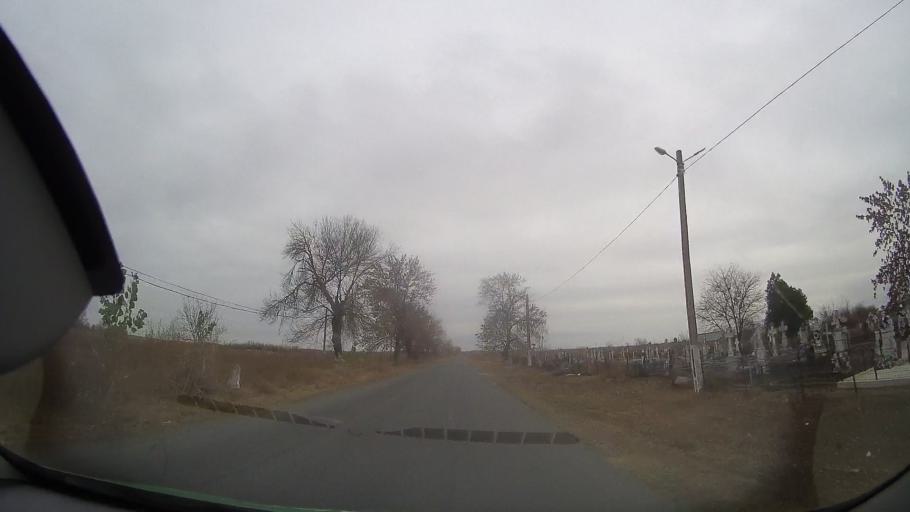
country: RO
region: Braila
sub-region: Comuna Ulmu
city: Ulmu
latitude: 44.9563
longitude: 27.3016
